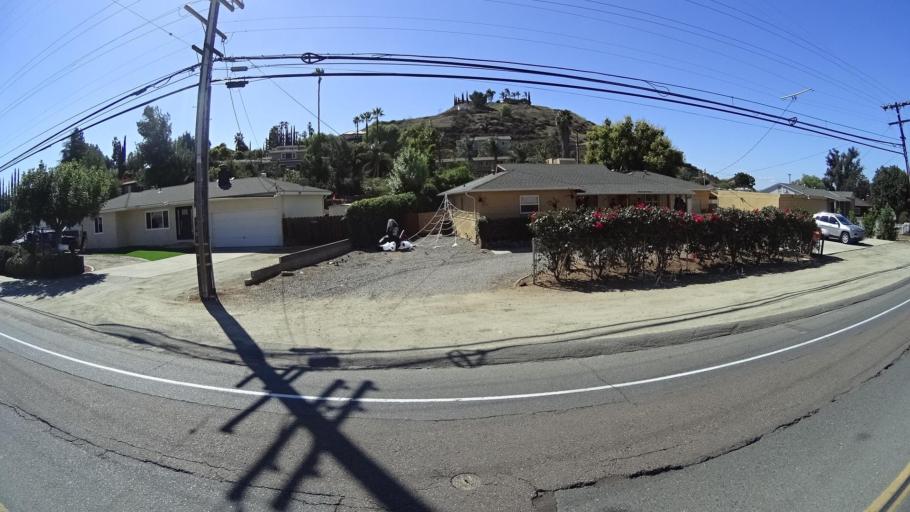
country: US
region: California
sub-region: San Diego County
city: Winter Gardens
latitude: 32.8212
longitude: -116.9395
